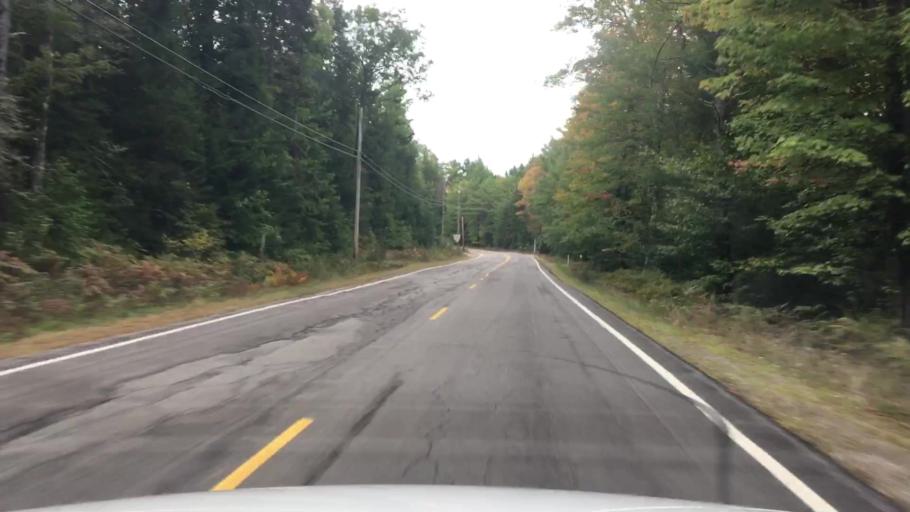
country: US
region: New Hampshire
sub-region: Carroll County
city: Effingham
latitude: 43.7488
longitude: -71.0030
